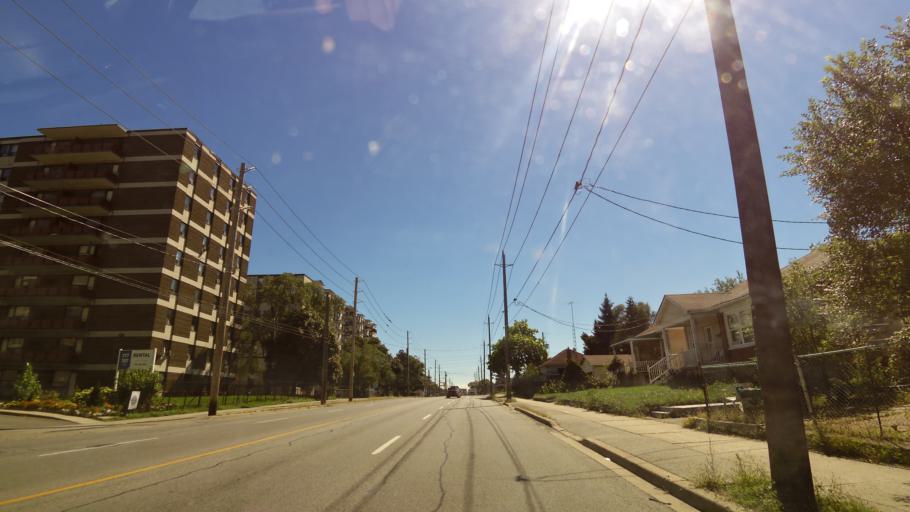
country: CA
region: Ontario
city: Etobicoke
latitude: 43.6734
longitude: -79.4945
